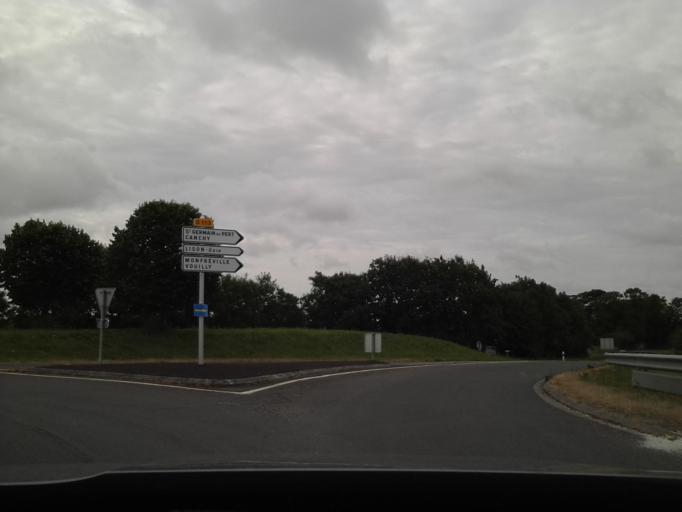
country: FR
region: Lower Normandy
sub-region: Departement du Calvados
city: Grandcamp-Maisy
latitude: 49.3370
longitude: -1.0093
